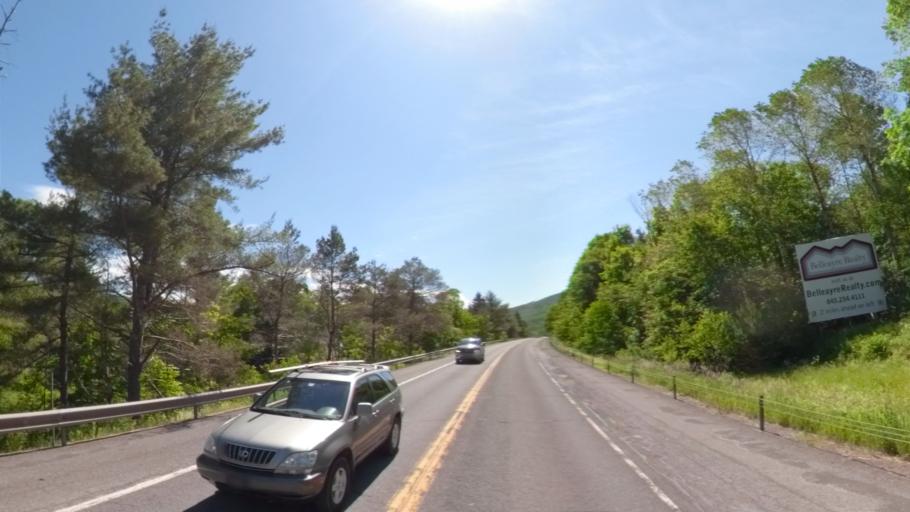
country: US
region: New York
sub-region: Delaware County
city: Stamford
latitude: 42.1585
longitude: -74.5559
